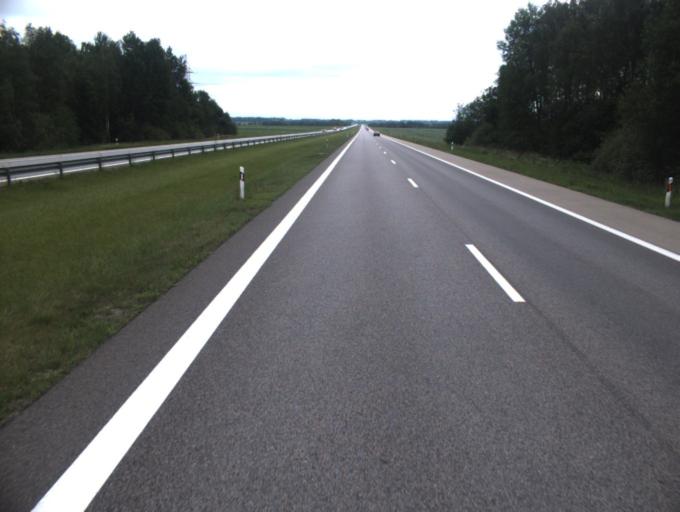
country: LT
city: Raseiniai
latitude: 55.3329
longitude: 23.1176
